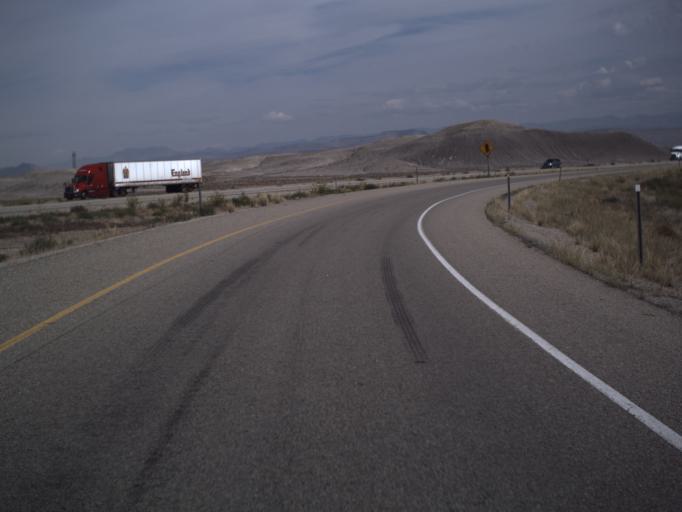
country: US
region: Utah
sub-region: Carbon County
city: East Carbon City
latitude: 38.9830
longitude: -110.2246
